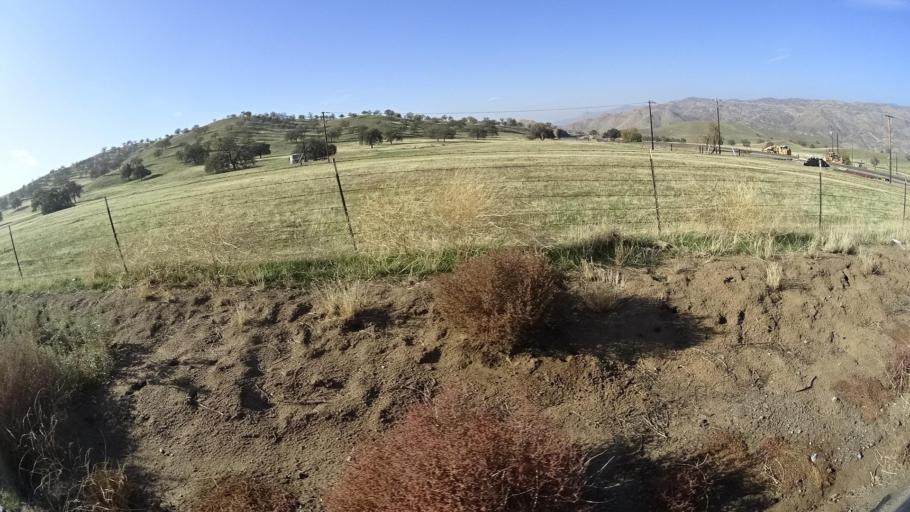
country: US
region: California
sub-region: Kern County
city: Bear Valley Springs
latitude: 35.2747
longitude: -118.6275
